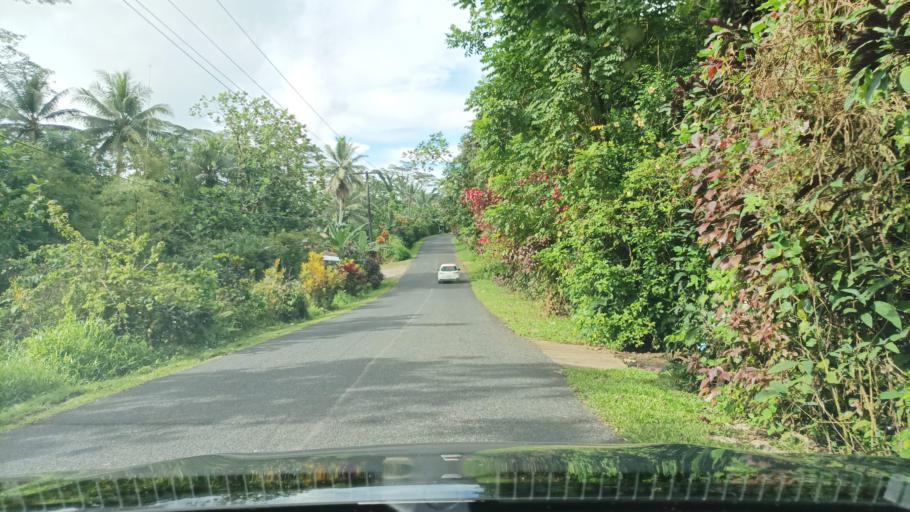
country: FM
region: Pohnpei
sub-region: Sokehs Municipality
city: Palikir - National Government Center
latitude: 6.9172
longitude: 158.1599
